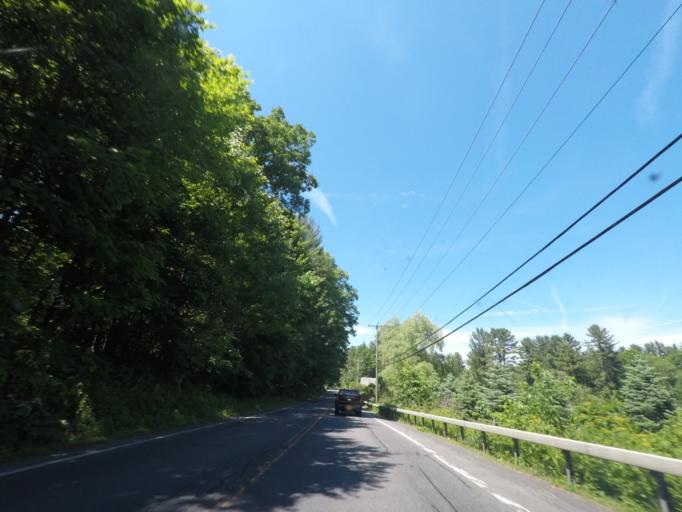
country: US
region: Massachusetts
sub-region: Berkshire County
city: Great Barrington
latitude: 42.2035
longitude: -73.5080
